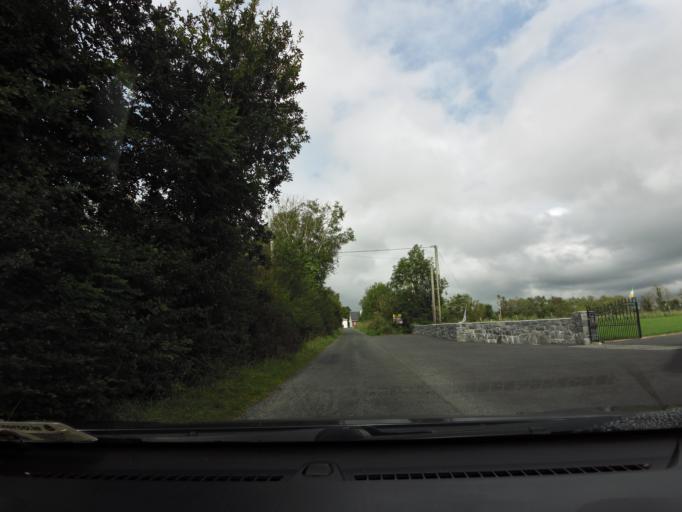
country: IE
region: Connaught
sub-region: County Galway
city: Loughrea
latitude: 53.3048
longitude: -8.6044
